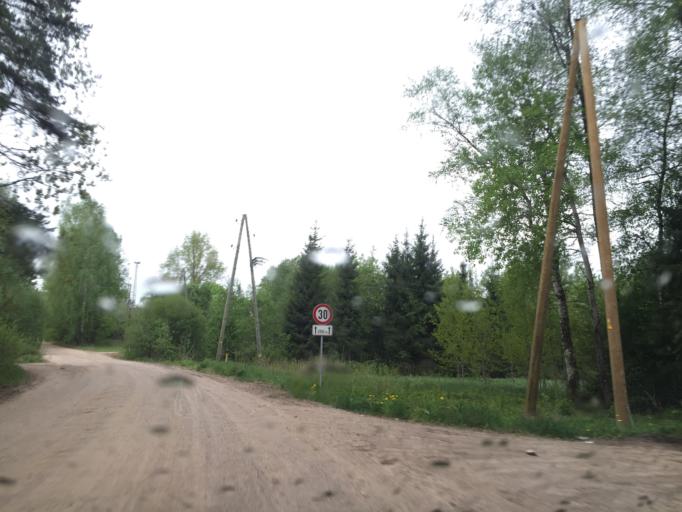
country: LV
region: Ogre
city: Ogre
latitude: 56.8258
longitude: 24.6512
